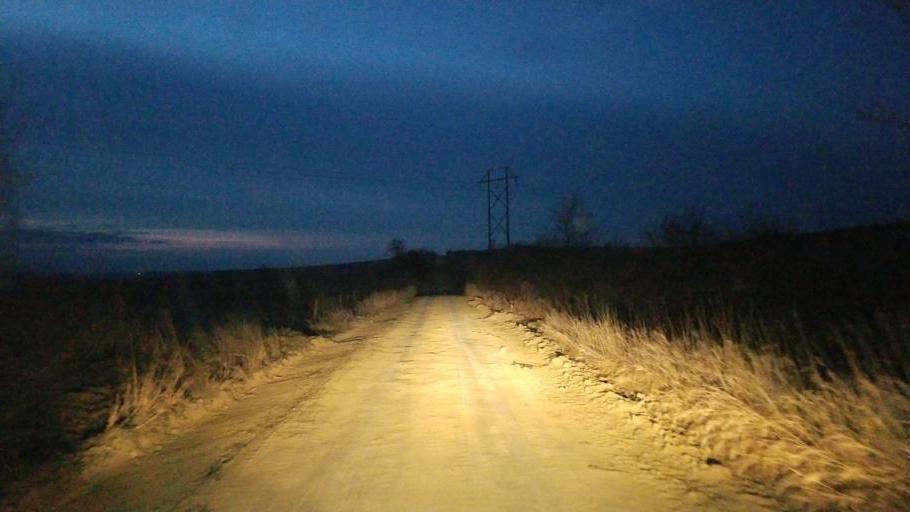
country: US
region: Nebraska
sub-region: Knox County
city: Center
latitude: 42.5709
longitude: -97.7985
